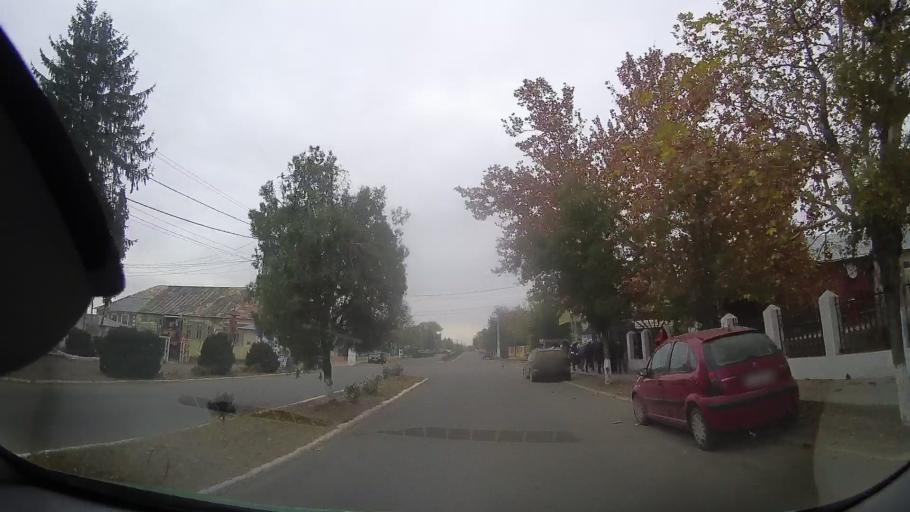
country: RO
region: Buzau
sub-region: Comuna Rusetu
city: Rusetu
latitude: 44.9620
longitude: 27.2167
